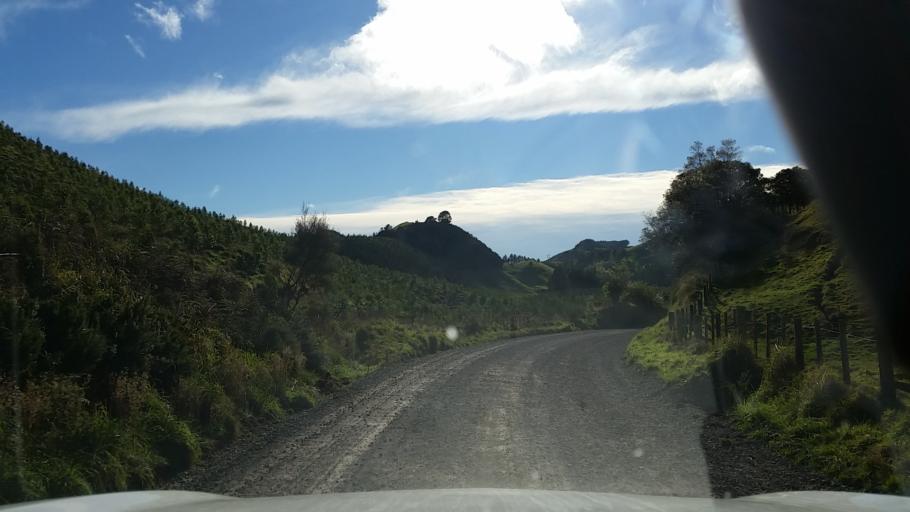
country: NZ
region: Bay of Plenty
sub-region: Rotorua District
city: Rotorua
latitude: -38.3633
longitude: 176.2080
